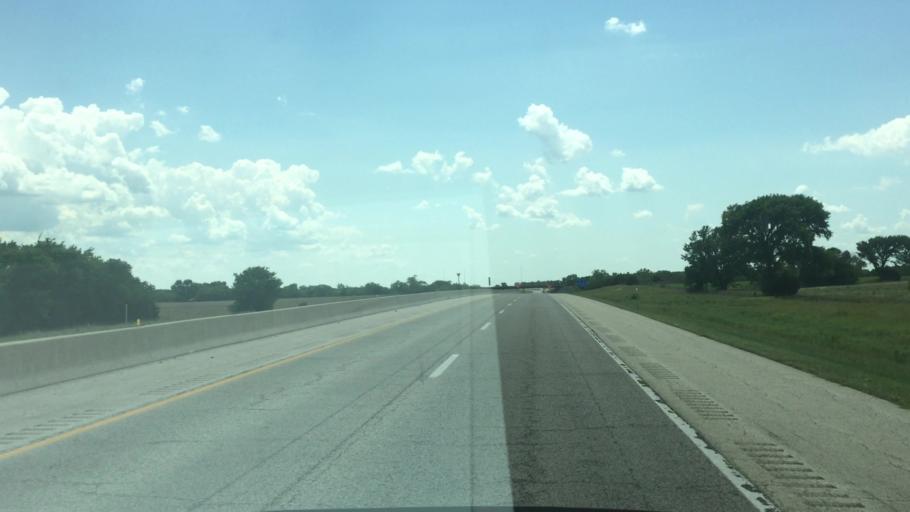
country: US
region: Kansas
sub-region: Lyon County
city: Emporia
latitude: 38.4823
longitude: -96.1739
